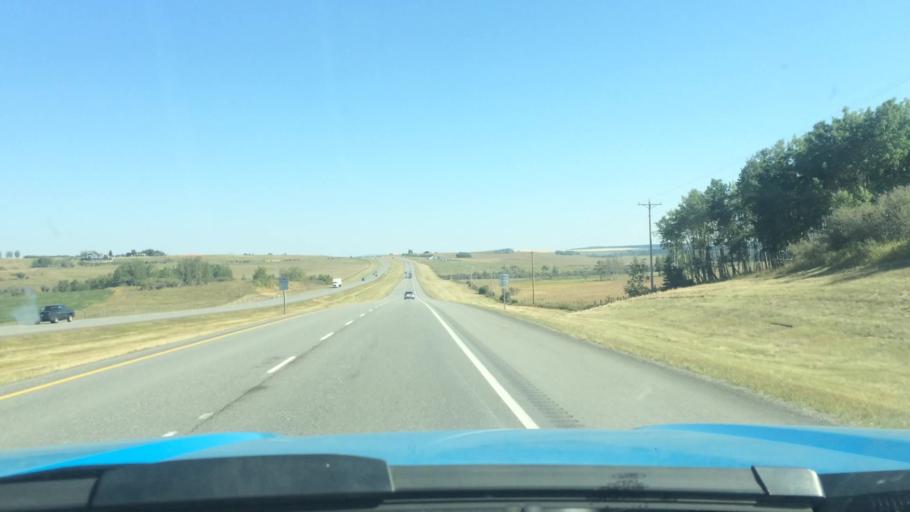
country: CA
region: Alberta
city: Cochrane
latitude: 51.0966
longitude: -114.5955
